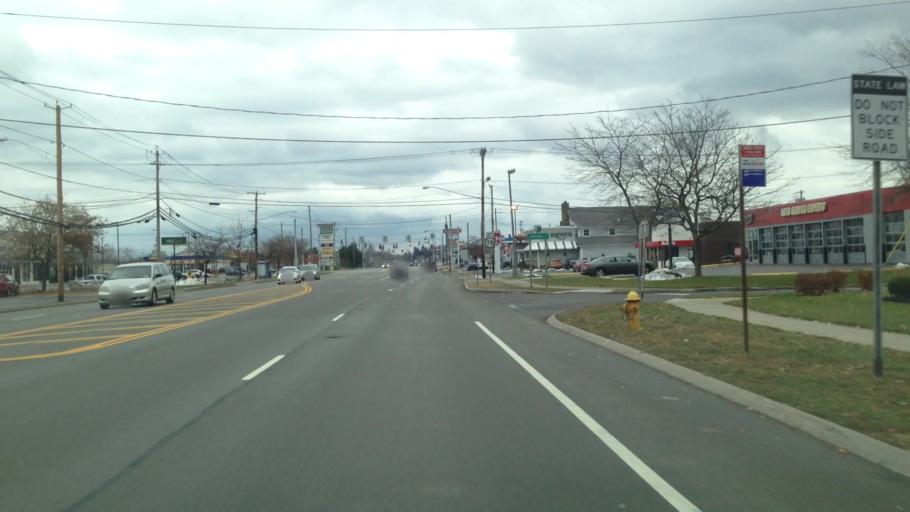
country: US
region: New York
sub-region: Erie County
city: Harris Hill
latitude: 42.9653
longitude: -78.6998
